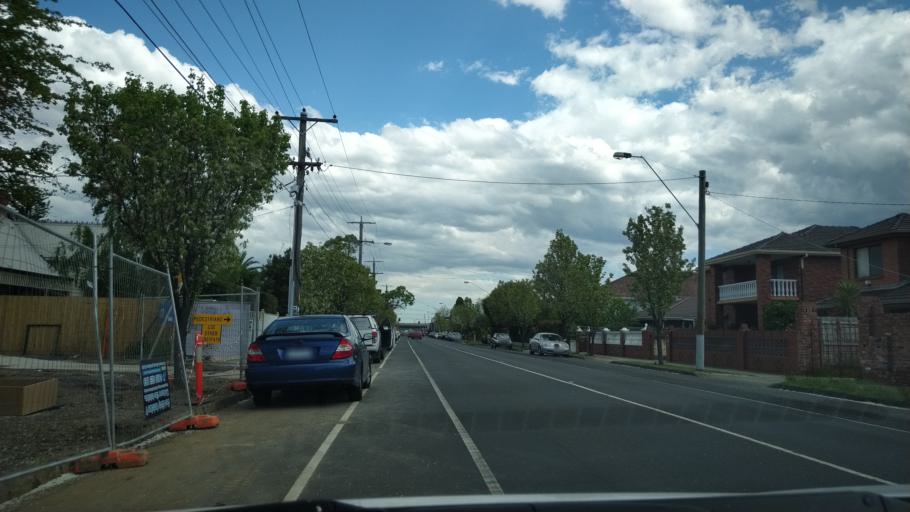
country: AU
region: Victoria
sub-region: Glen Eira
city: Carnegie
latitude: -37.8813
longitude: 145.0586
